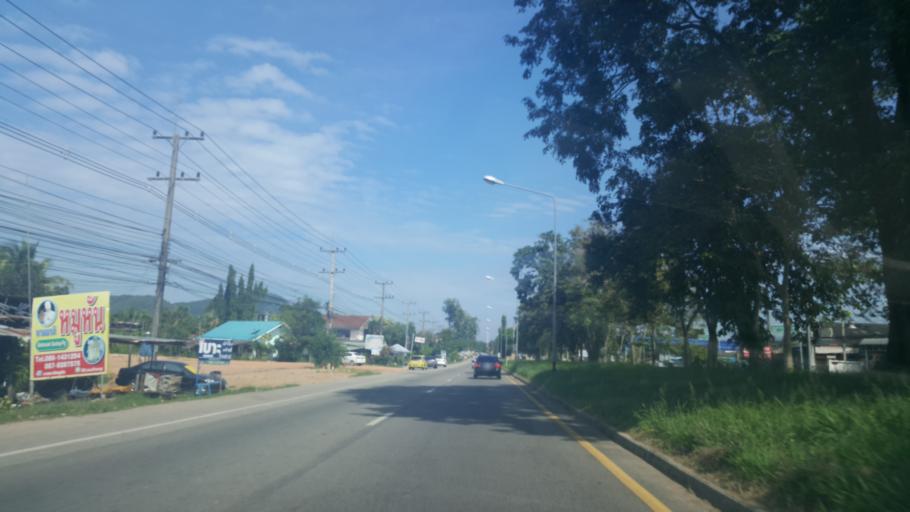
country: TH
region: Chon Buri
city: Sattahip
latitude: 12.7115
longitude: 100.8886
